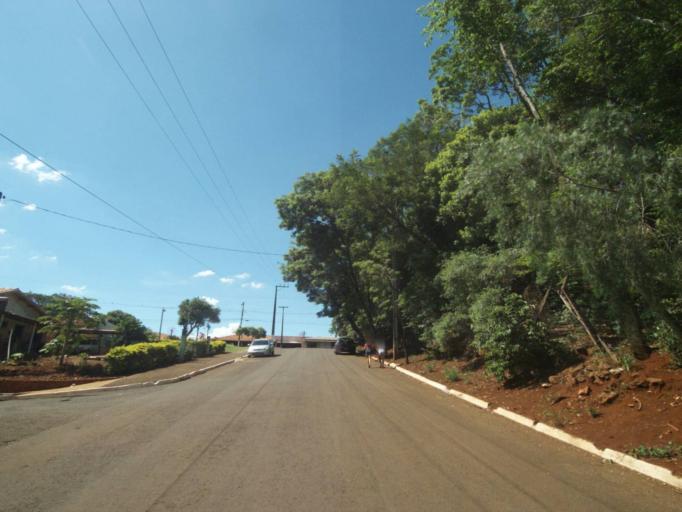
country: BR
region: Parana
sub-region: Sertanopolis
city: Sertanopolis
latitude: -23.0443
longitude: -50.8205
